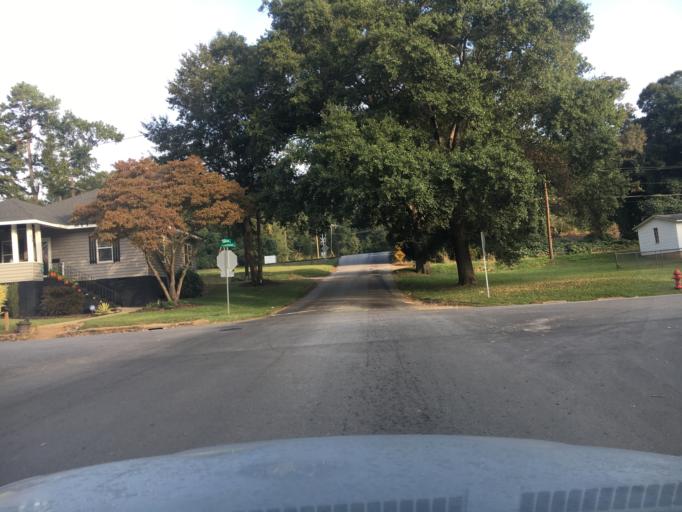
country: US
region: South Carolina
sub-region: Spartanburg County
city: Lyman
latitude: 34.9471
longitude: -82.1307
